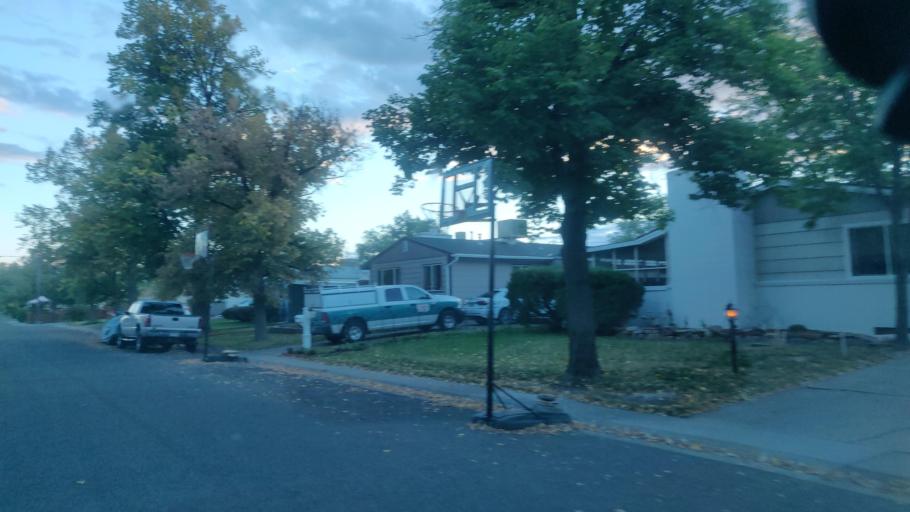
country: US
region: Colorado
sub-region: Mesa County
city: Grand Junction
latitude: 39.0837
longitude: -108.5408
